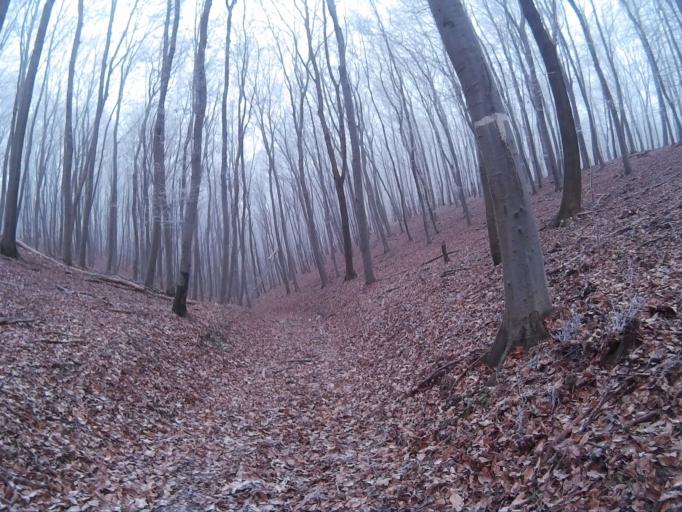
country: HU
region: Komarom-Esztergom
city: Oroszlany
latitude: 47.4393
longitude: 18.3651
